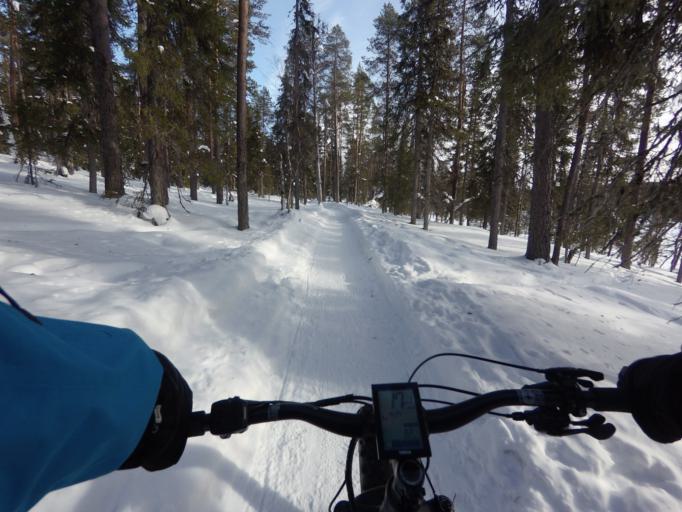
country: FI
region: Lapland
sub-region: Tunturi-Lappi
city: Kolari
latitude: 67.5996
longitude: 24.2480
